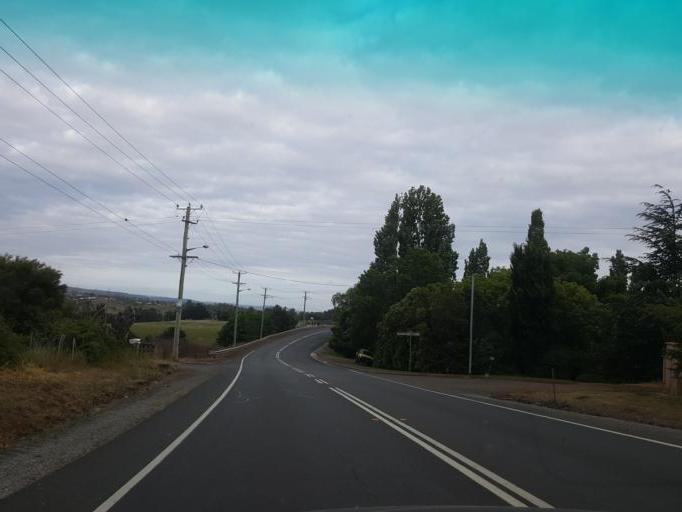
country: AU
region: Tasmania
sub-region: Launceston
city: Newstead
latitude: -41.4675
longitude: 147.2081
